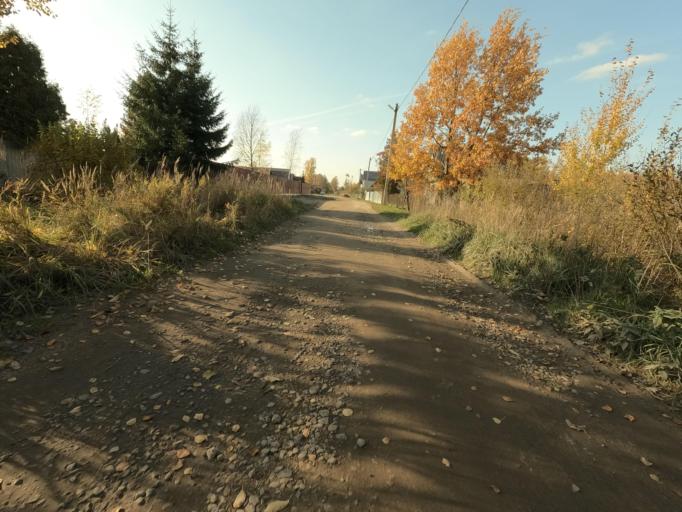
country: RU
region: Leningrad
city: Mga
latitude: 59.7472
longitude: 31.0684
